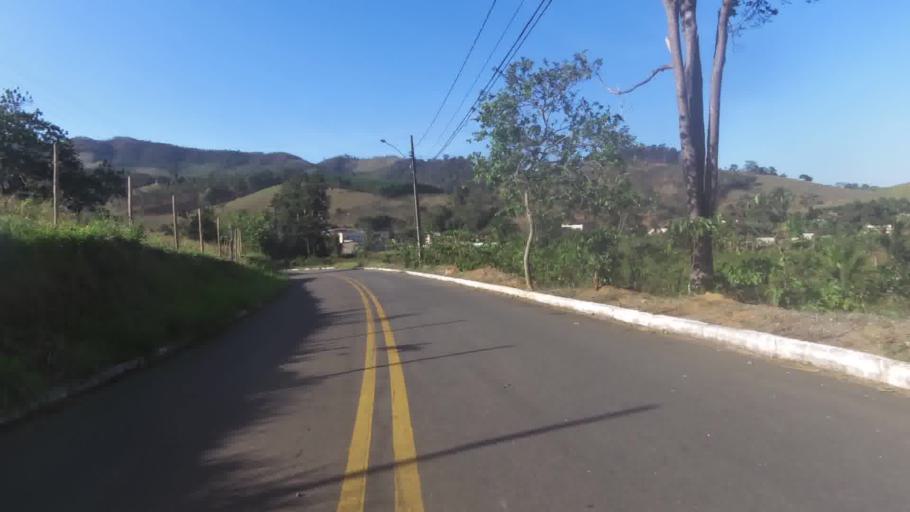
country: BR
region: Espirito Santo
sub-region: Iconha
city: Iconha
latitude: -20.7327
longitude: -40.7793
